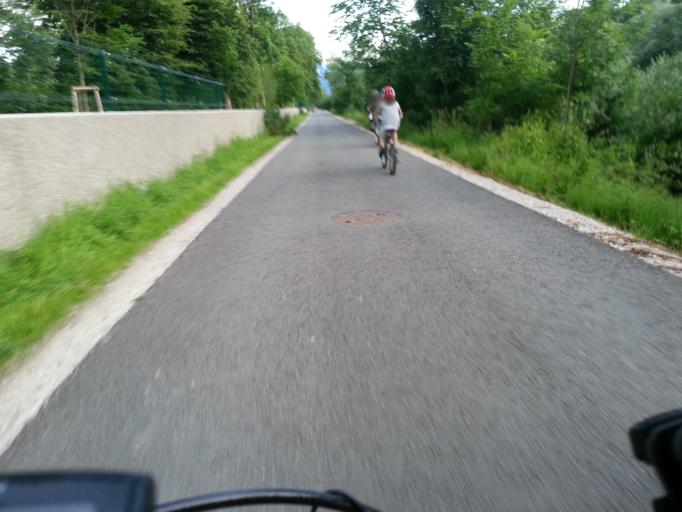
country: AT
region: Salzburg
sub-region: Politischer Bezirk Salzburg-Umgebung
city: Elsbethen
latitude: 47.7805
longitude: 13.0767
